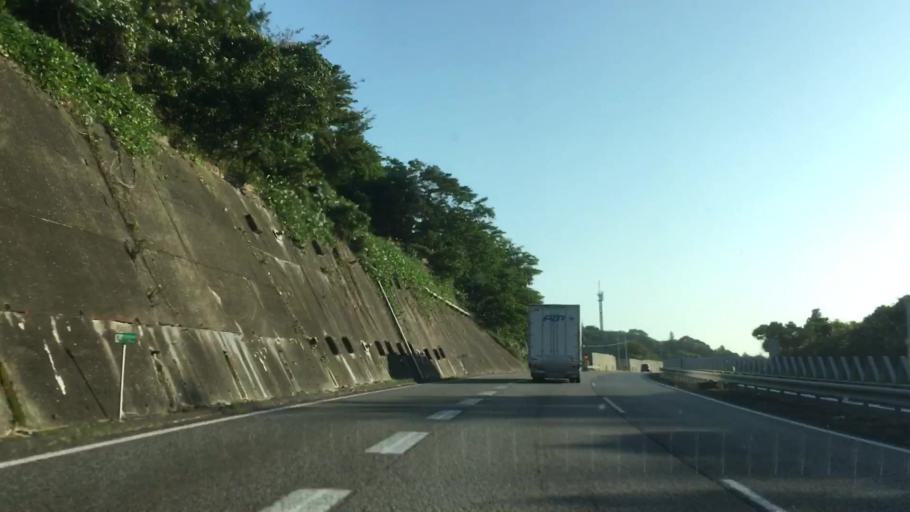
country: JP
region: Yamaguchi
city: Onoda
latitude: 34.1479
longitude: 131.2338
